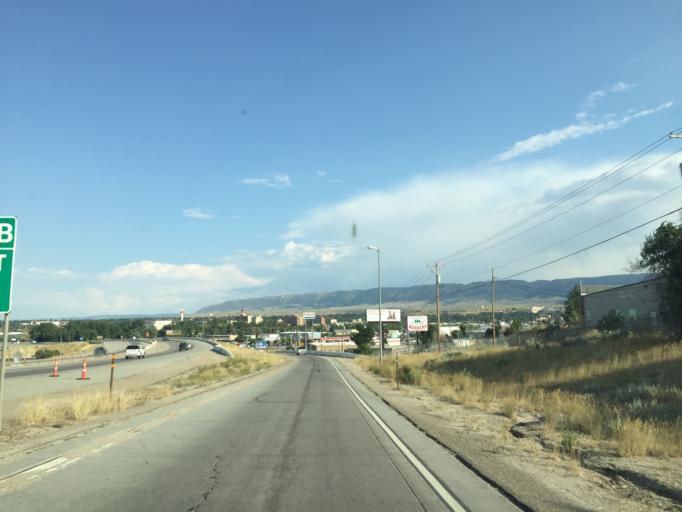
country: US
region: Wyoming
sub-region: Natrona County
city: Casper
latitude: 42.8594
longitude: -106.3371
